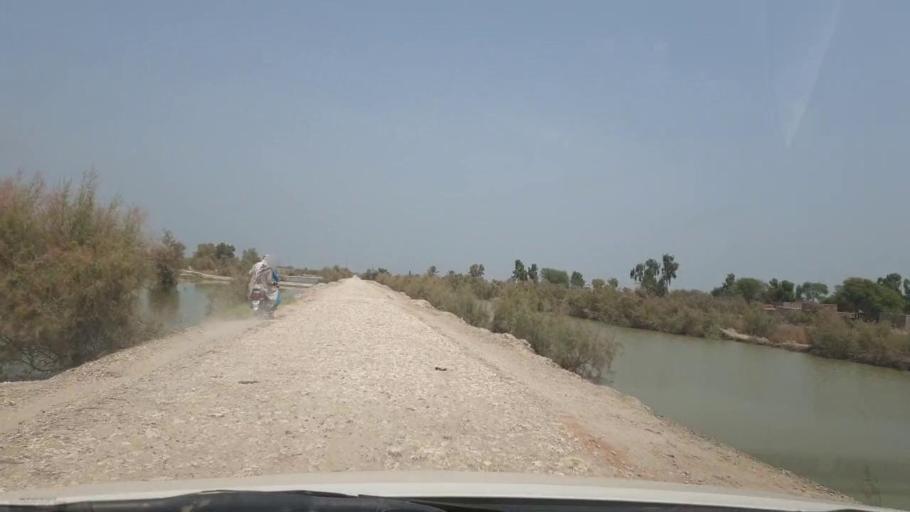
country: PK
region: Sindh
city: Rustam jo Goth
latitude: 28.0578
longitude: 68.8163
